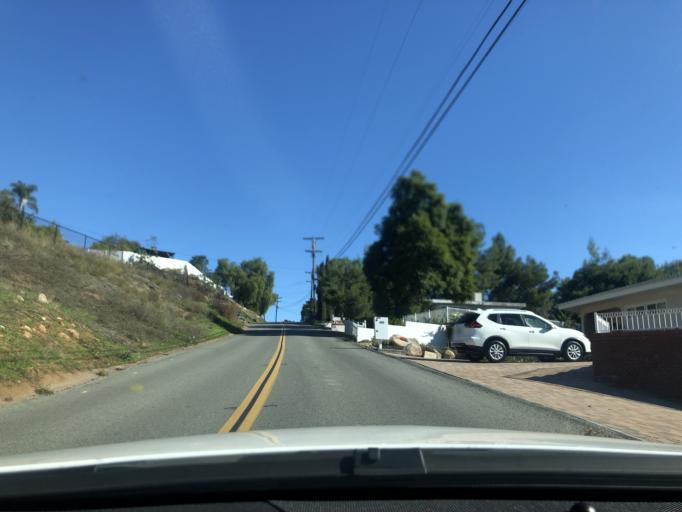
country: US
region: California
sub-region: San Diego County
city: El Cajon
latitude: 32.7831
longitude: -116.9444
